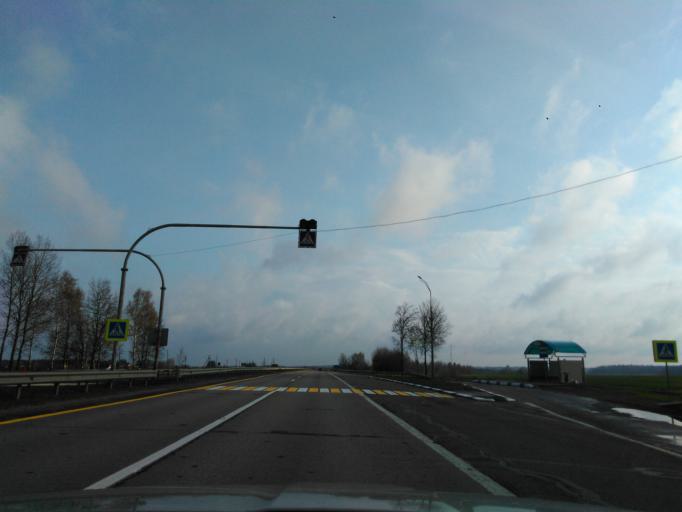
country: BY
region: Minsk
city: Lahoysk
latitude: 54.1651
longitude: 27.8167
